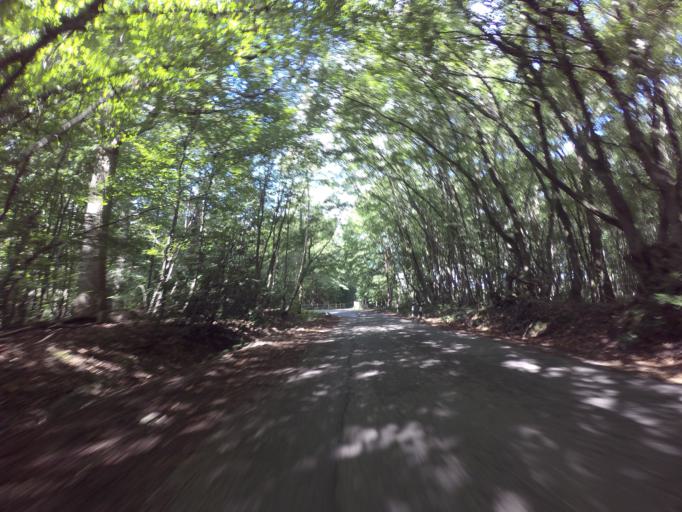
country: GB
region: England
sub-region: Kent
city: Staplehurst
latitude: 51.1341
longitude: 0.5711
